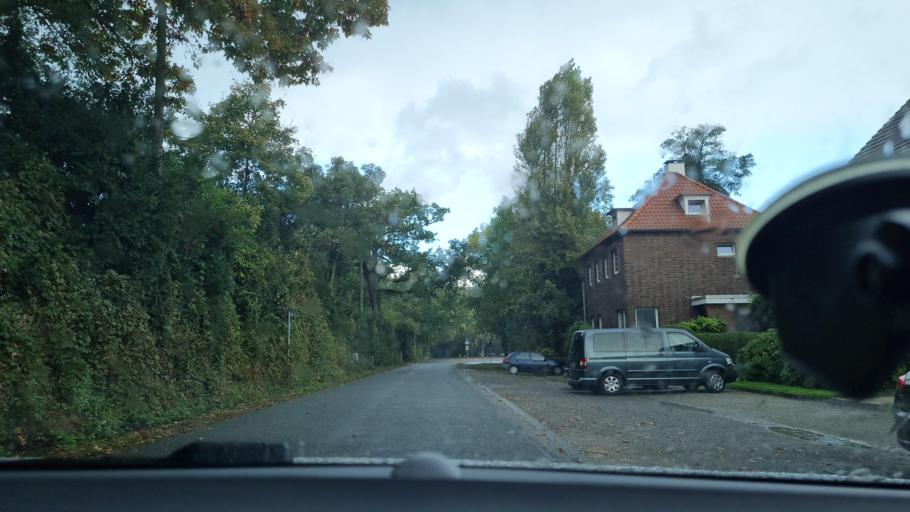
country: DE
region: North Rhine-Westphalia
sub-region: Regierungsbezirk Dusseldorf
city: Dinslaken
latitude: 51.5534
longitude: 6.7326
